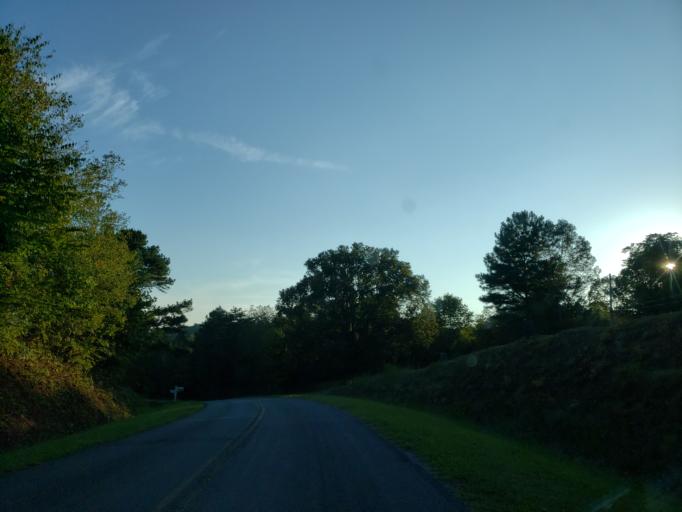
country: US
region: Georgia
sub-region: Gilmer County
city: Ellijay
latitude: 34.6571
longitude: -84.3374
